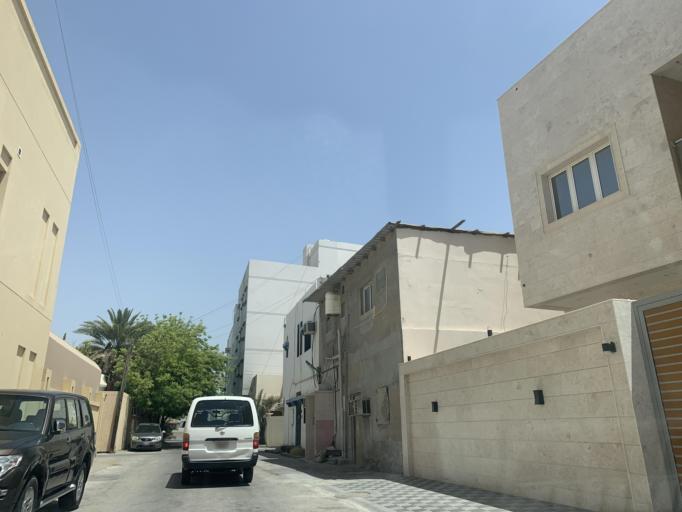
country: BH
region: Northern
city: Sitrah
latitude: 26.1604
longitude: 50.6193
